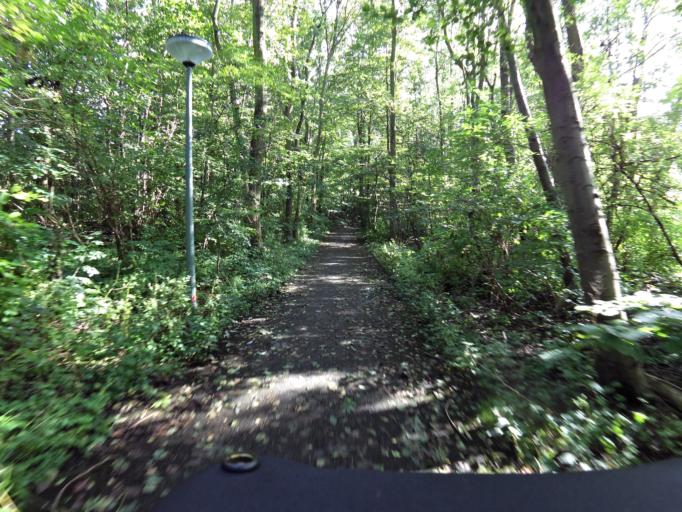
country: NL
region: South Holland
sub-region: Gemeente Vlaardingen
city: Vlaardingen
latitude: 51.9394
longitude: 4.3488
